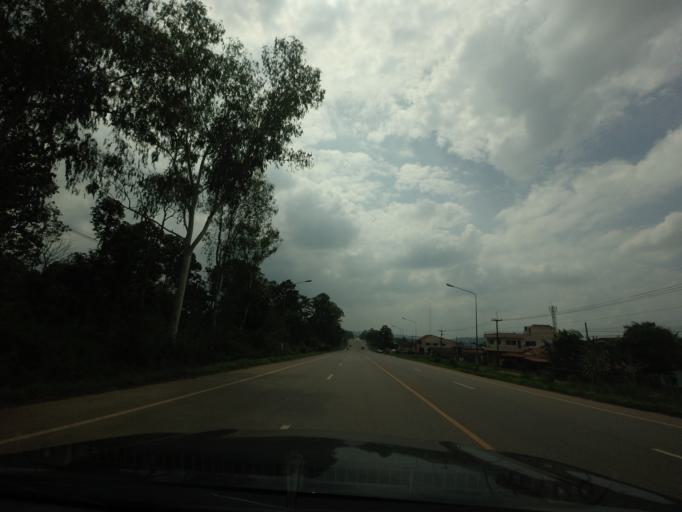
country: TH
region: Loei
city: Dan Sai
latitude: 17.3644
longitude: 101.2556
